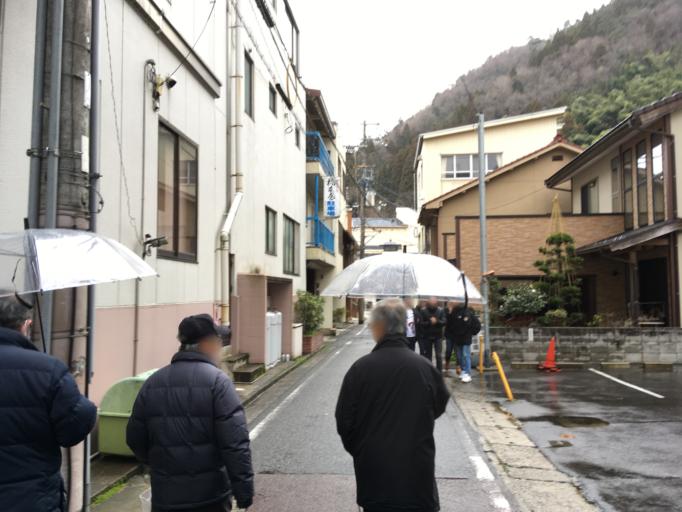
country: JP
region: Tottori
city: Tottori
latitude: 35.5560
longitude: 134.4880
